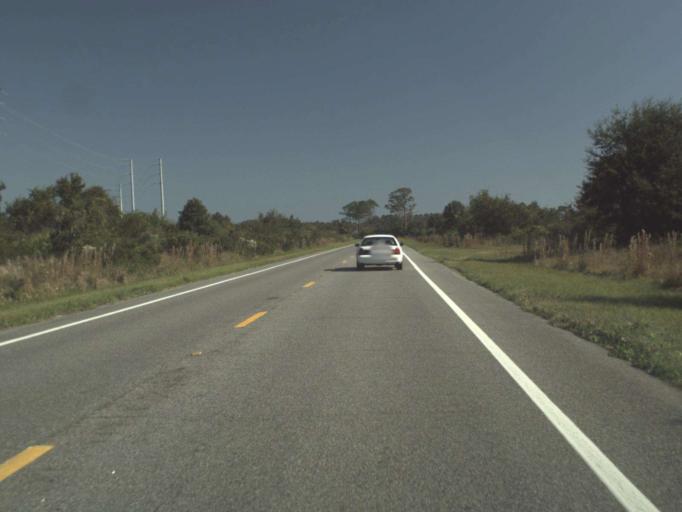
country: US
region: Florida
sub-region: Franklin County
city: Apalachicola
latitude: 29.7207
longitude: -85.0685
